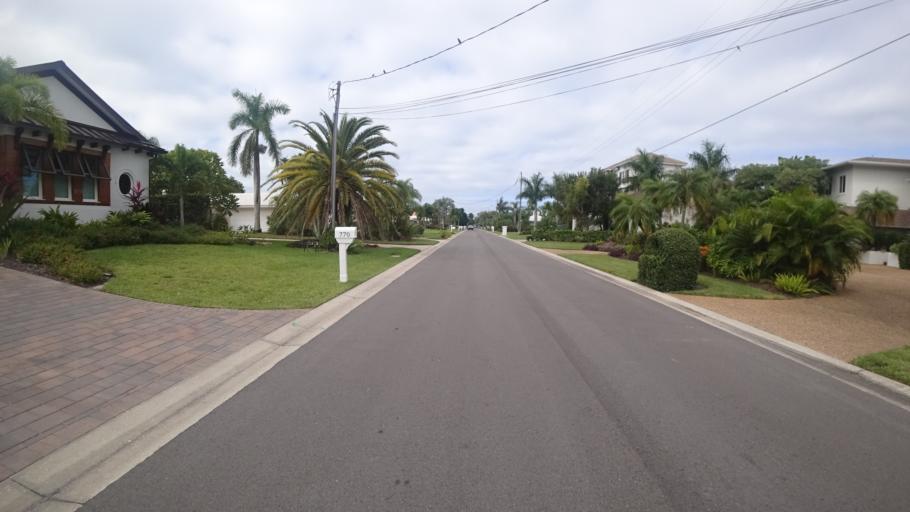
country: US
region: Florida
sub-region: Manatee County
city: Longboat Key
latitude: 27.4218
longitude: -82.6626
